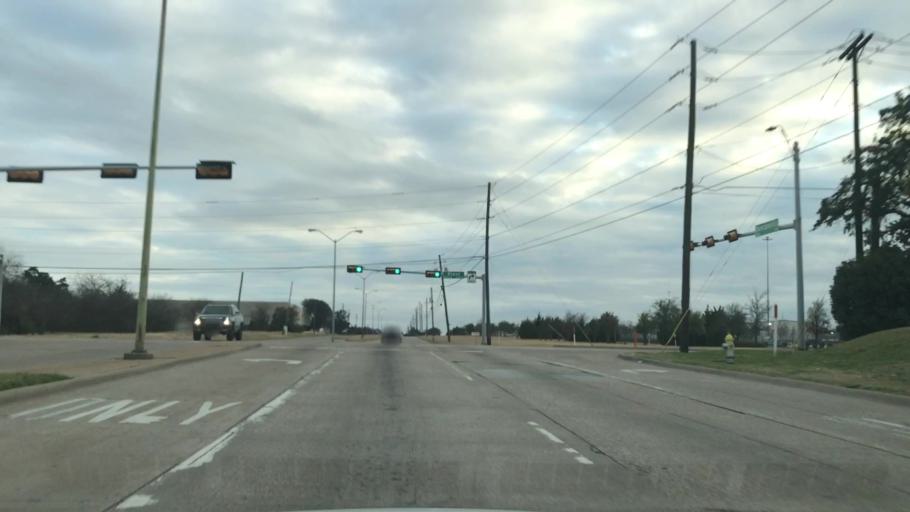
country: US
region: Texas
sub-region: Dallas County
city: Cockrell Hill
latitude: 32.7061
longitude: -96.9088
